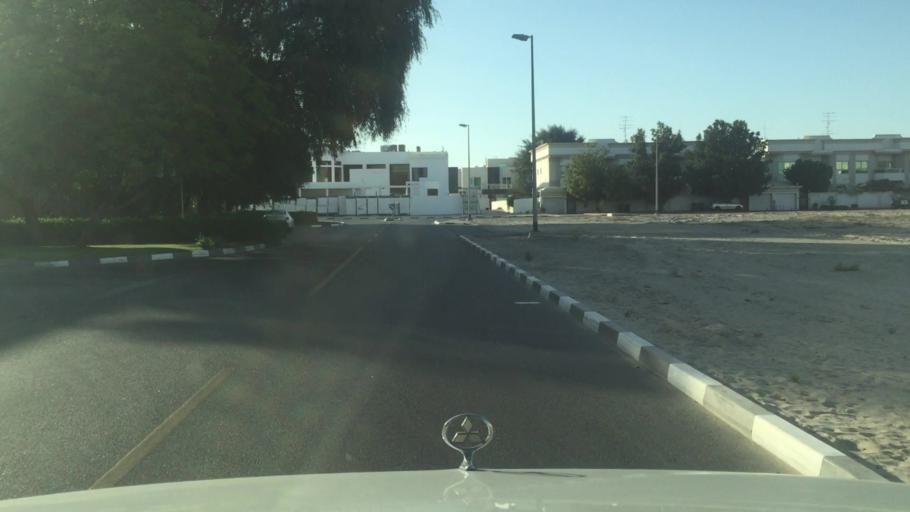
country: AE
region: Dubai
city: Dubai
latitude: 25.1627
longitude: 55.2275
